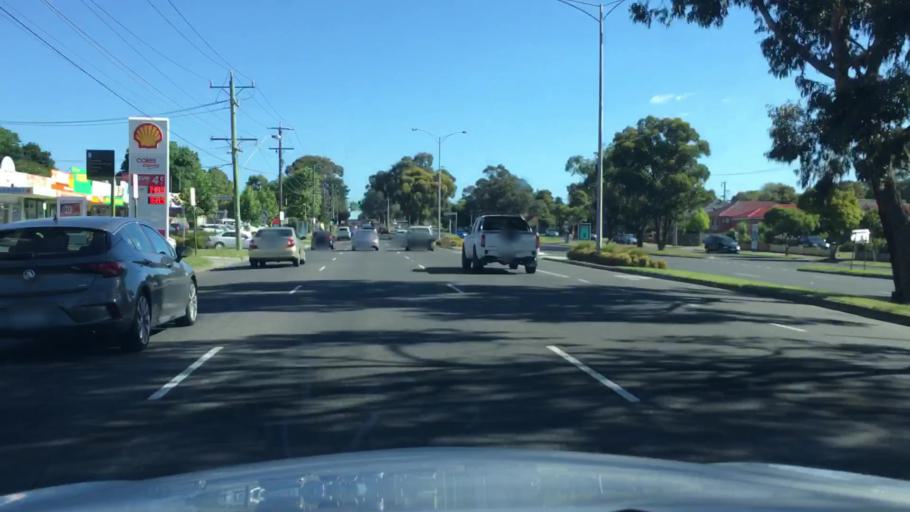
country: AU
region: Victoria
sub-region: Whitehorse
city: Forest Hill
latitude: -37.8406
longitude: 145.1716
